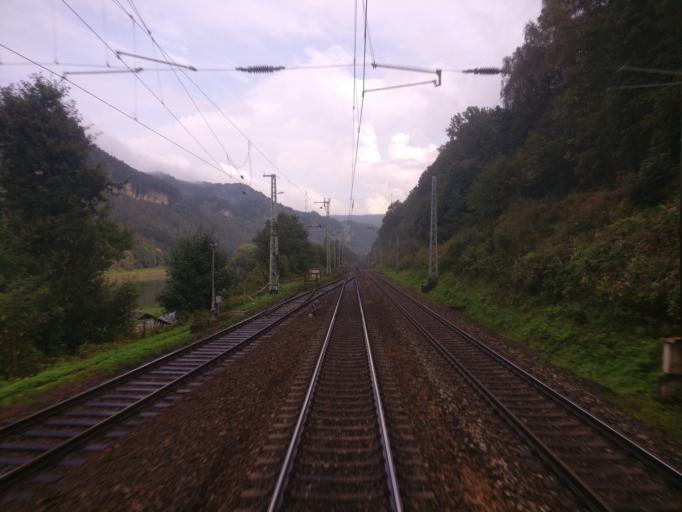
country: DE
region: Saxony
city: Bad Schandau
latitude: 50.9076
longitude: 14.1876
